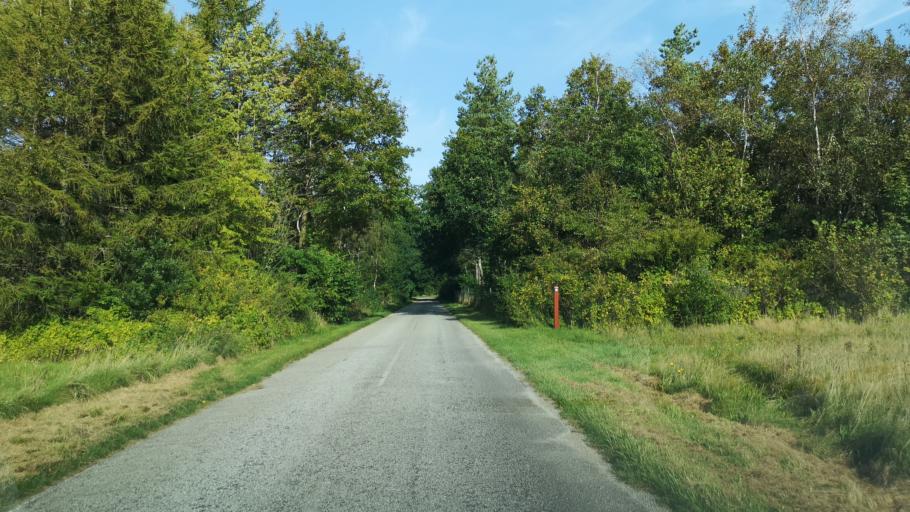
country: DK
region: Central Jutland
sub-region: Herning Kommune
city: Herning
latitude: 56.1758
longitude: 8.9527
